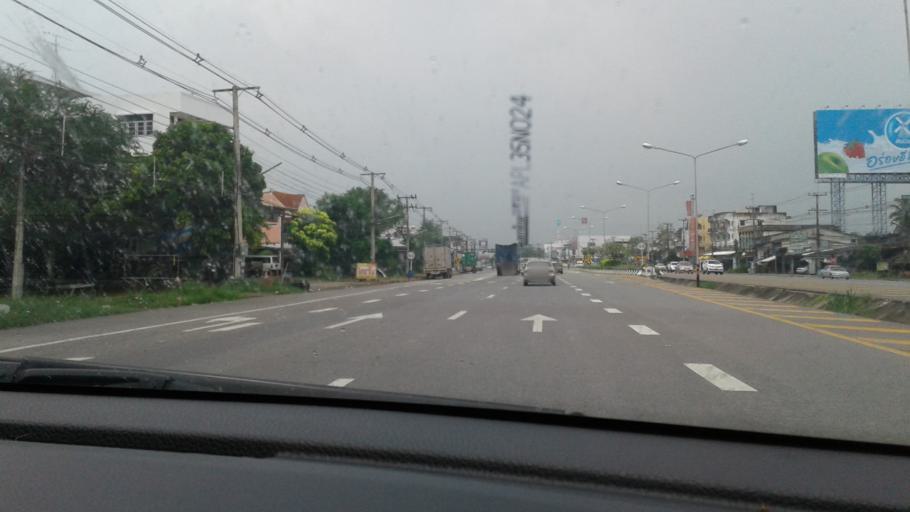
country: TH
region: Prachuap Khiri Khan
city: Kui Buri
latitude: 12.0645
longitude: 99.8595
